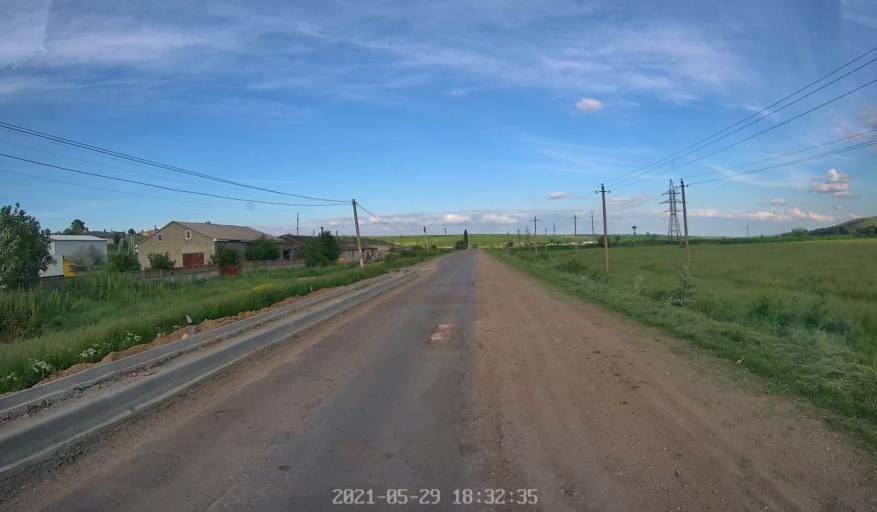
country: MD
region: Chisinau
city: Singera
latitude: 46.8175
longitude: 28.8946
